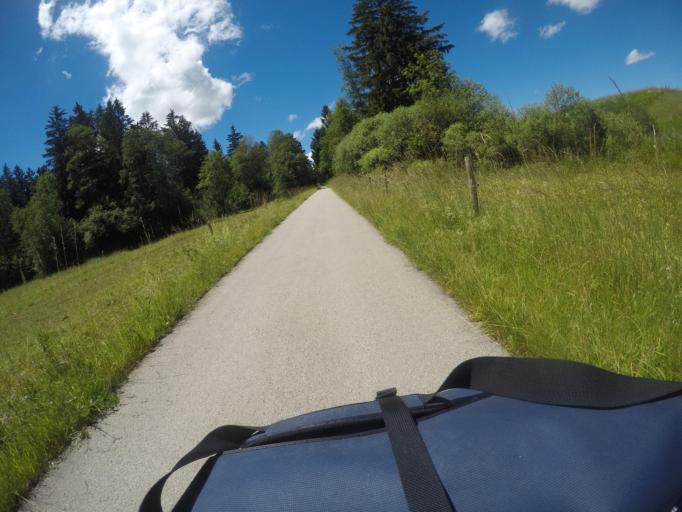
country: DE
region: Bavaria
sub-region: Swabia
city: Lechbruck
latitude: 47.6957
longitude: 10.7848
